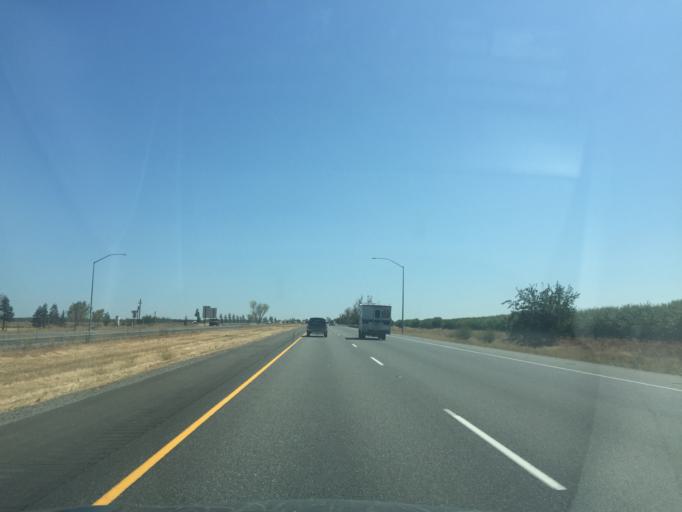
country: US
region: California
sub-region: Tehama County
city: Corning
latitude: 39.9975
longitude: -122.2055
